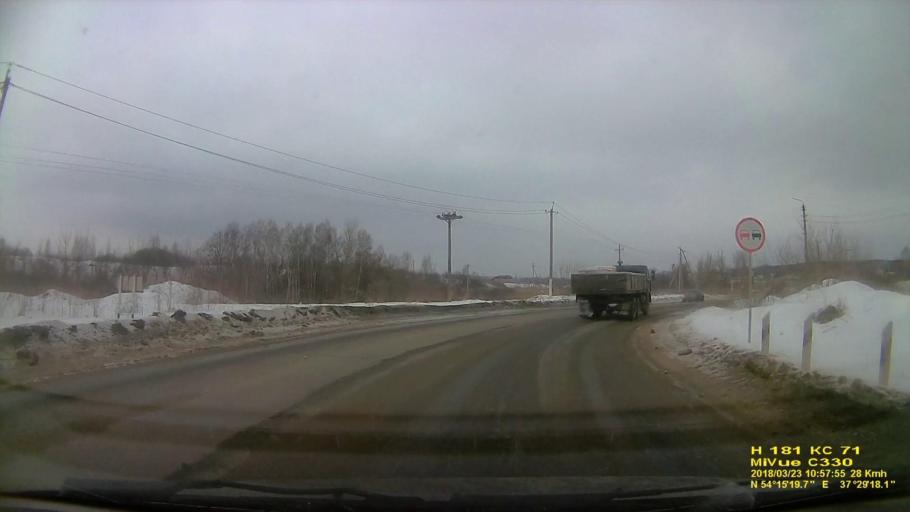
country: RU
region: Tula
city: Barsuki
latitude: 54.2556
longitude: 37.4881
